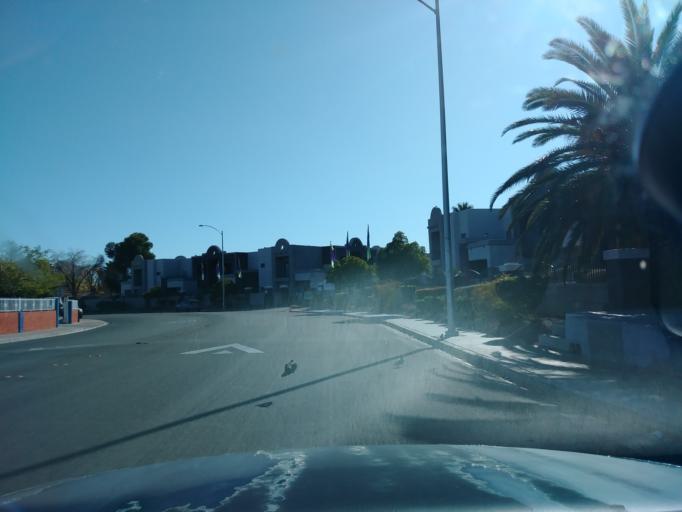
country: US
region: Nevada
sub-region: Clark County
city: Spring Valley
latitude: 36.1779
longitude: -115.2409
